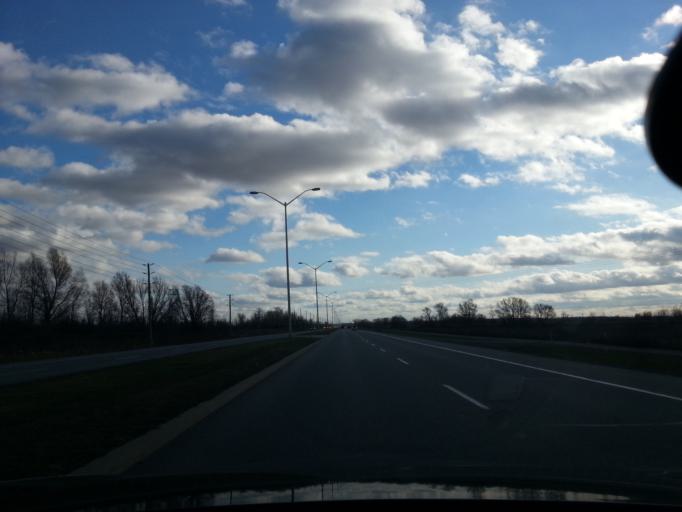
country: CA
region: Ontario
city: Ottawa
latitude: 45.3112
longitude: -75.6845
